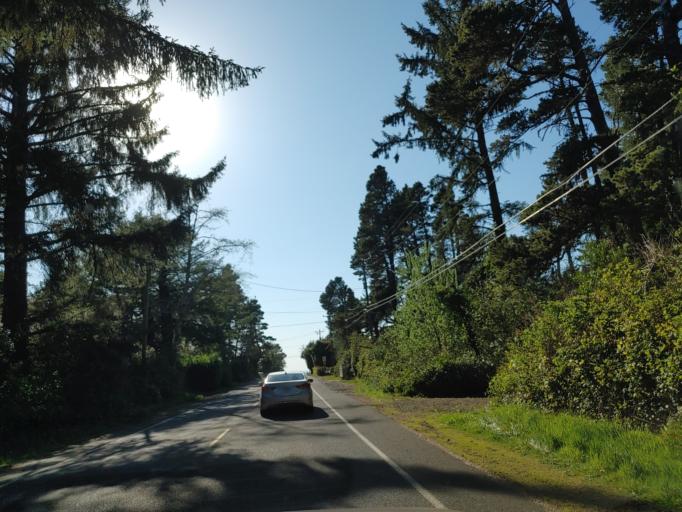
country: US
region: Oregon
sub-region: Lincoln County
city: Depoe Bay
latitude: 44.7471
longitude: -124.0585
